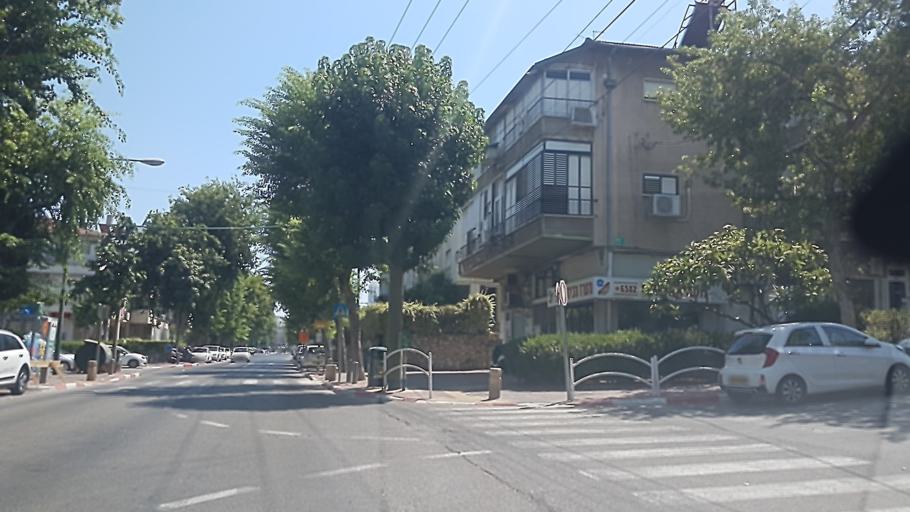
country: IL
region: Tel Aviv
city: Bene Beraq
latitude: 32.0815
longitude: 34.8257
